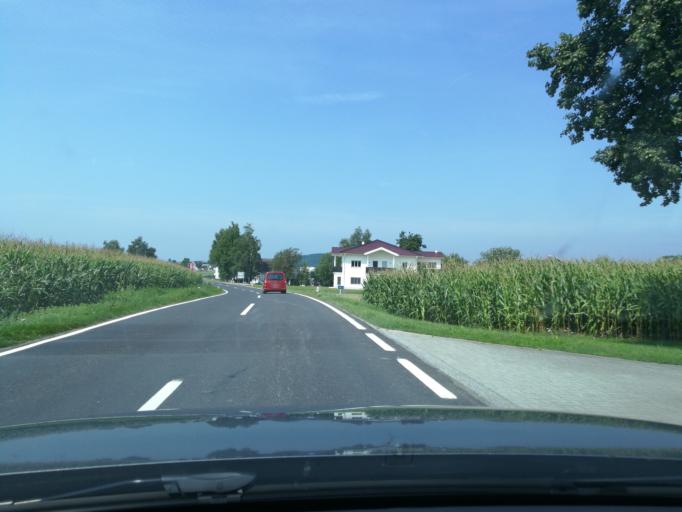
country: AT
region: Upper Austria
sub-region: Politischer Bezirk Grieskirchen
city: Grieskirchen
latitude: 48.3560
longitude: 13.7013
